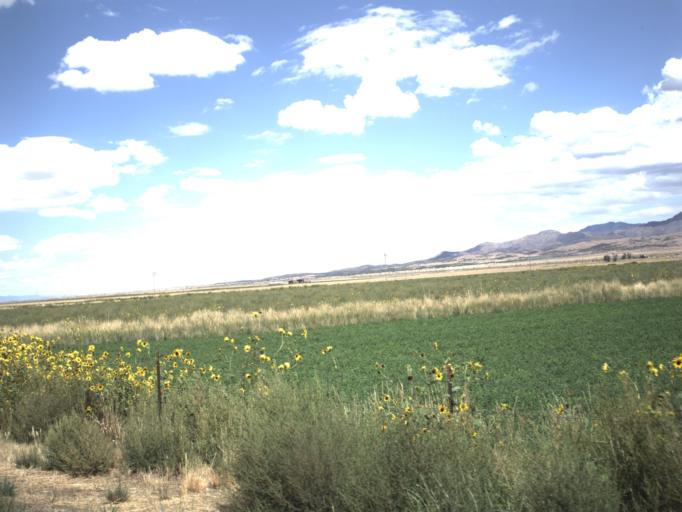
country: US
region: Utah
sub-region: Millard County
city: Delta
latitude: 39.2133
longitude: -112.4160
